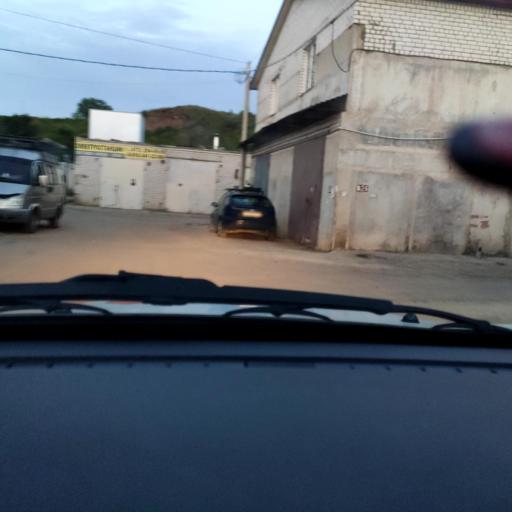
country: RU
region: Voronezj
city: Pridonskoy
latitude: 51.6403
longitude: 39.1187
